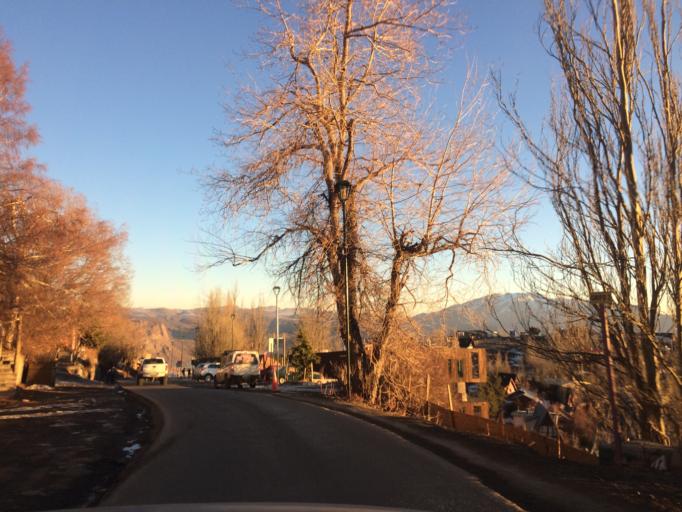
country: CL
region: Santiago Metropolitan
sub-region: Provincia de Santiago
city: Villa Presidente Frei, Nunoa, Santiago, Chile
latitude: -33.3498
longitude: -70.3085
